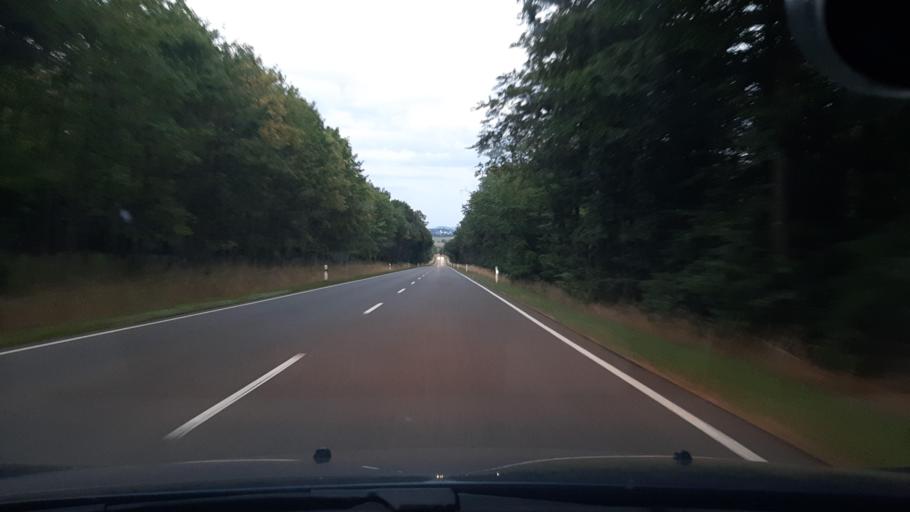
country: DE
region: North Rhine-Westphalia
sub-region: Regierungsbezirk Koln
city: Nettersheim
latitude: 50.4483
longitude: 6.5779
